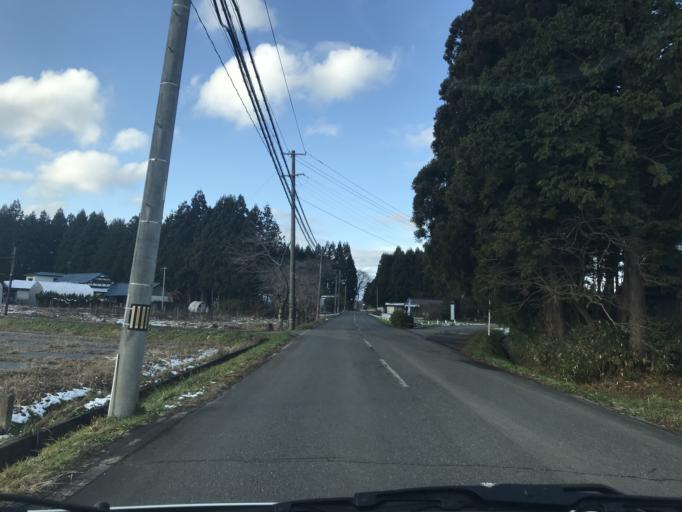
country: JP
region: Iwate
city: Kitakami
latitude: 39.2196
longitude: 141.0457
